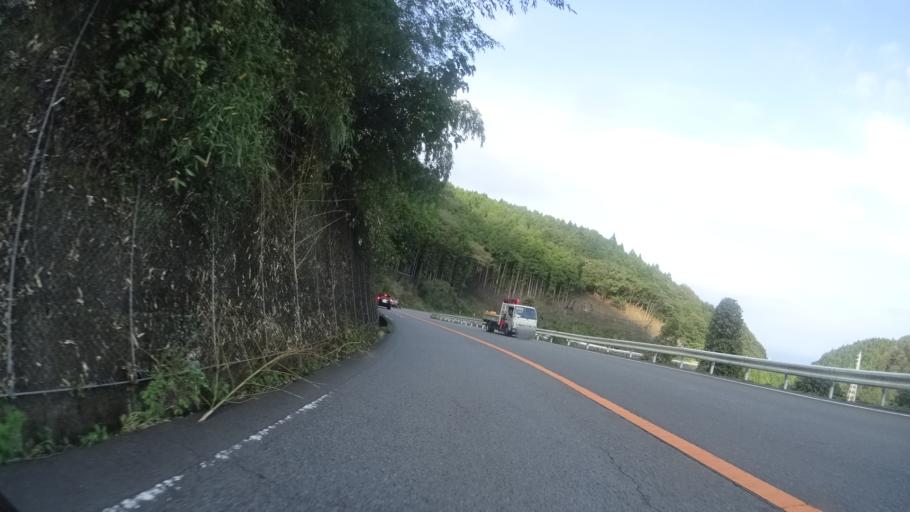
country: JP
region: Oita
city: Beppu
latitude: 33.2841
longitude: 131.4531
